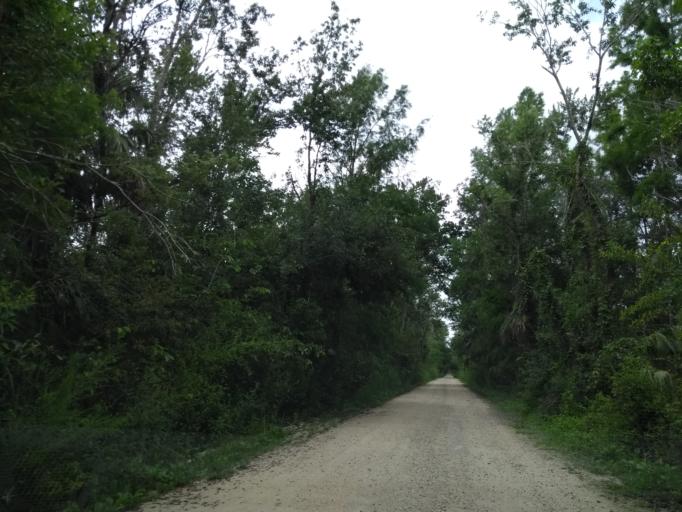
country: US
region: Florida
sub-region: Collier County
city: Lely Resort
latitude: 25.9867
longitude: -81.4110
